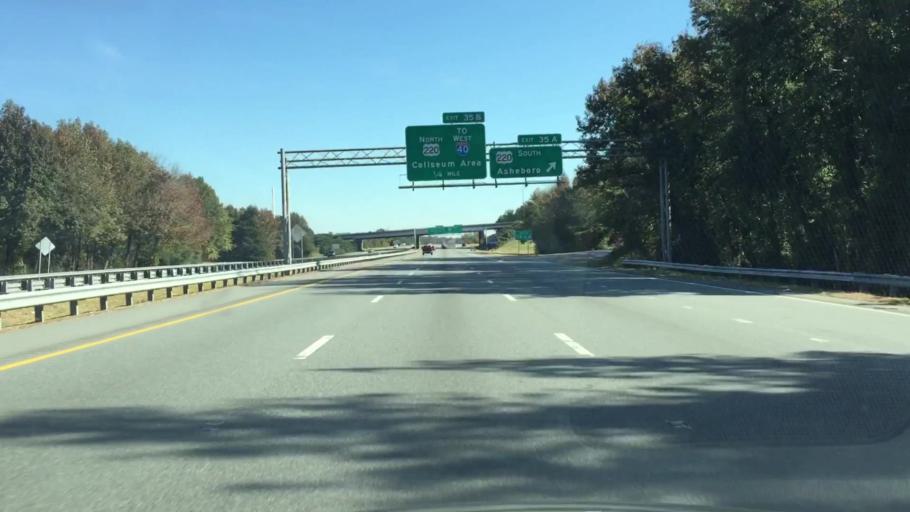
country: US
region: North Carolina
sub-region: Guilford County
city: Greensboro
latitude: 36.0166
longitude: -79.8298
